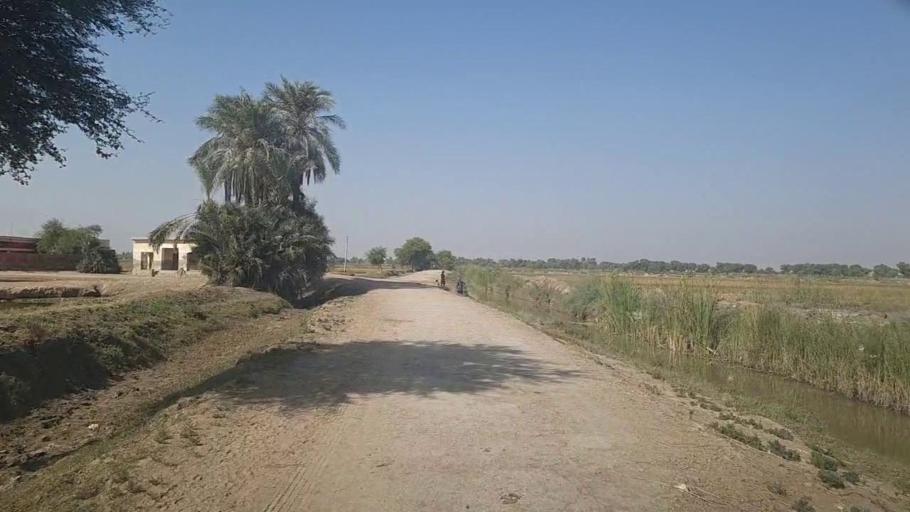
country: PK
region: Sindh
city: Thul
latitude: 28.3115
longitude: 68.7679
